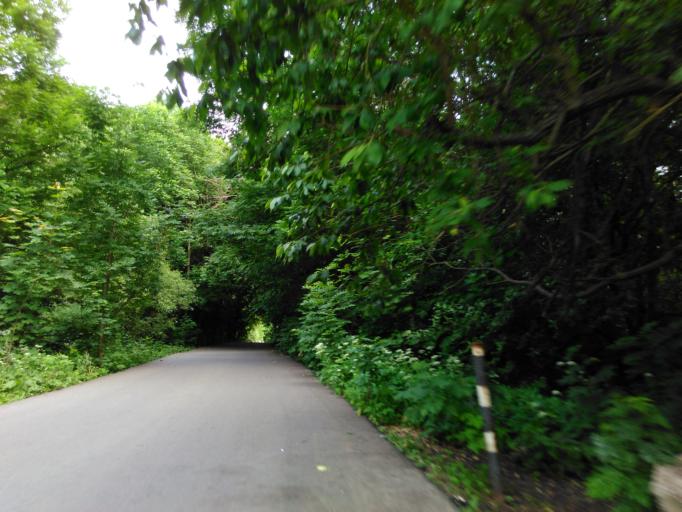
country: RU
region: Moscow
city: Yasenevo
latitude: 55.6224
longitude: 37.5396
